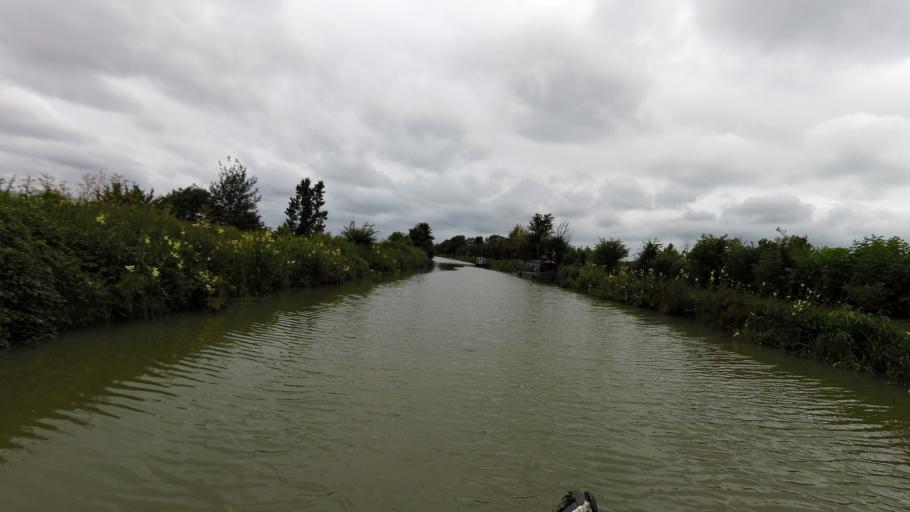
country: GB
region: England
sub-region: Wiltshire
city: Melksham
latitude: 51.3468
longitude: -2.1308
